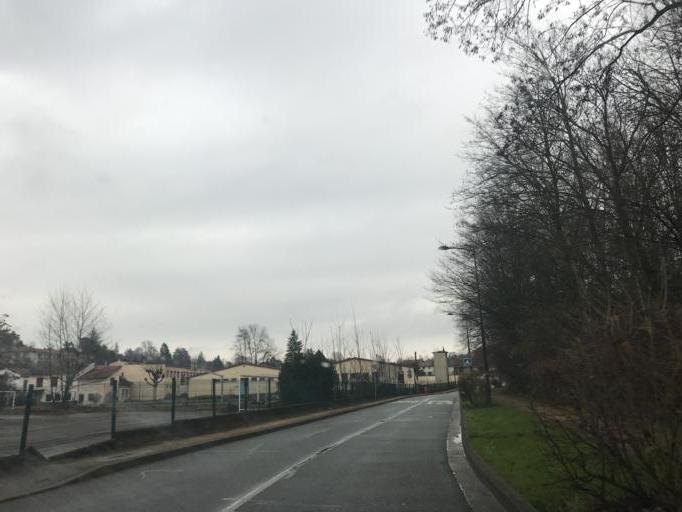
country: FR
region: Rhone-Alpes
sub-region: Departement du Rhone
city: Fontaines-sur-Saone
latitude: 45.8398
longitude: 4.8447
